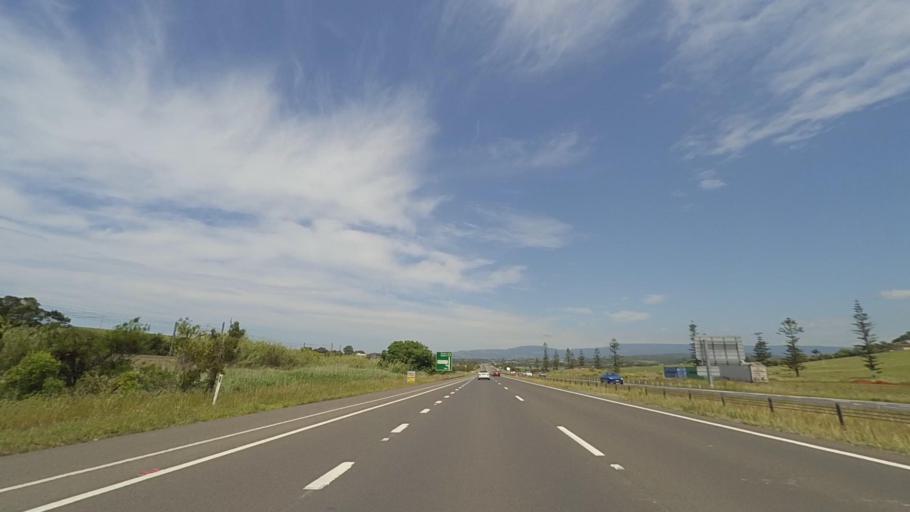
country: AU
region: New South Wales
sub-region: Shellharbour
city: Croom
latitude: -34.5944
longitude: 150.8430
